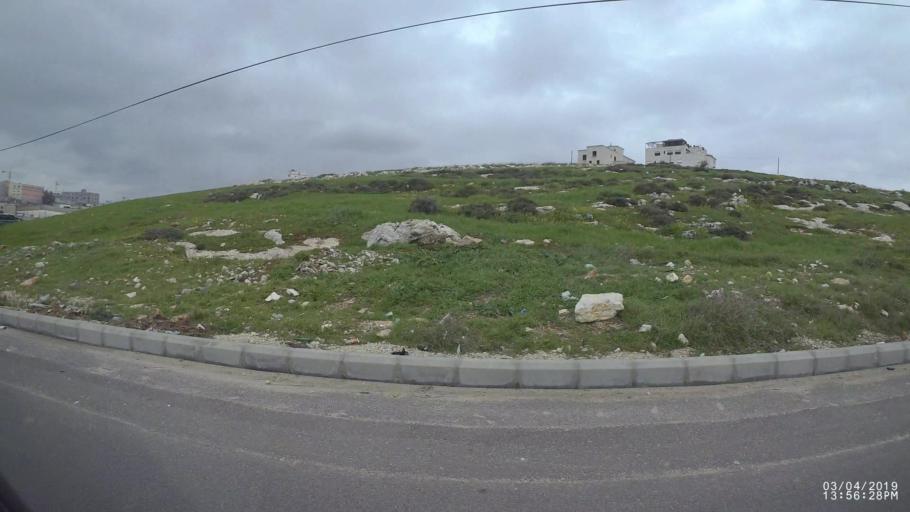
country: JO
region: Amman
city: Wadi as Sir
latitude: 31.9323
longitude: 35.8482
